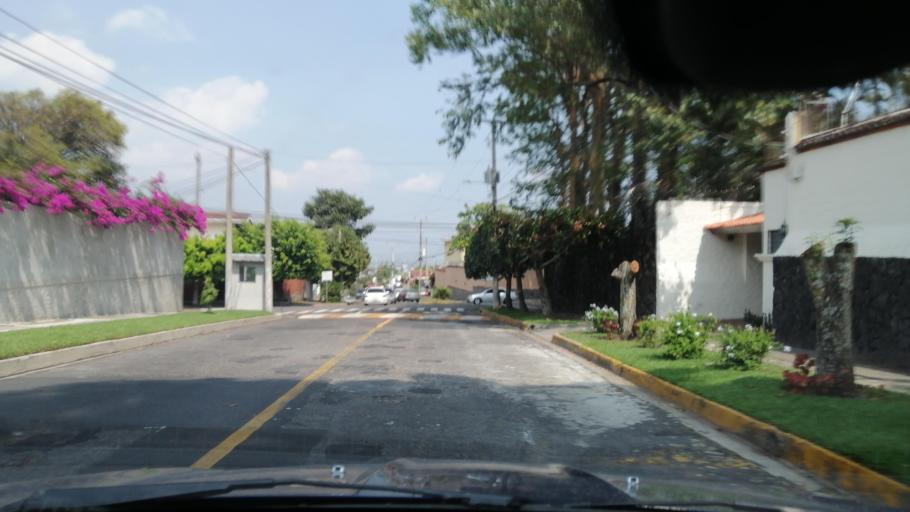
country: SV
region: La Libertad
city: Antiguo Cuscatlan
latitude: 13.6983
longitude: -89.2458
